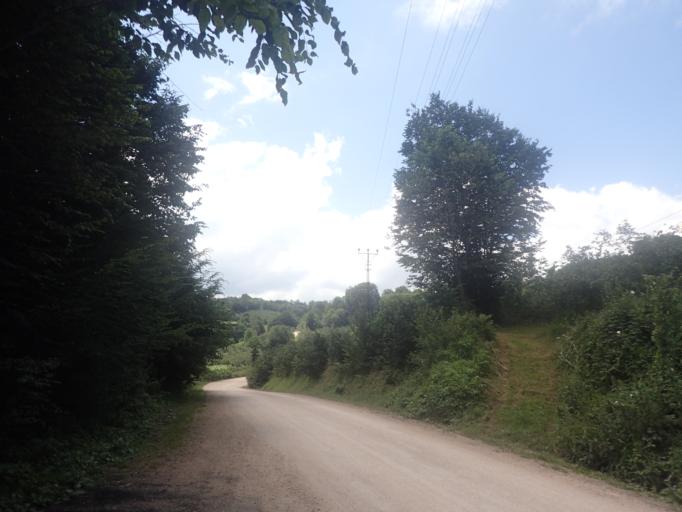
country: TR
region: Ordu
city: Aybasti
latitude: 40.7260
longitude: 37.3439
